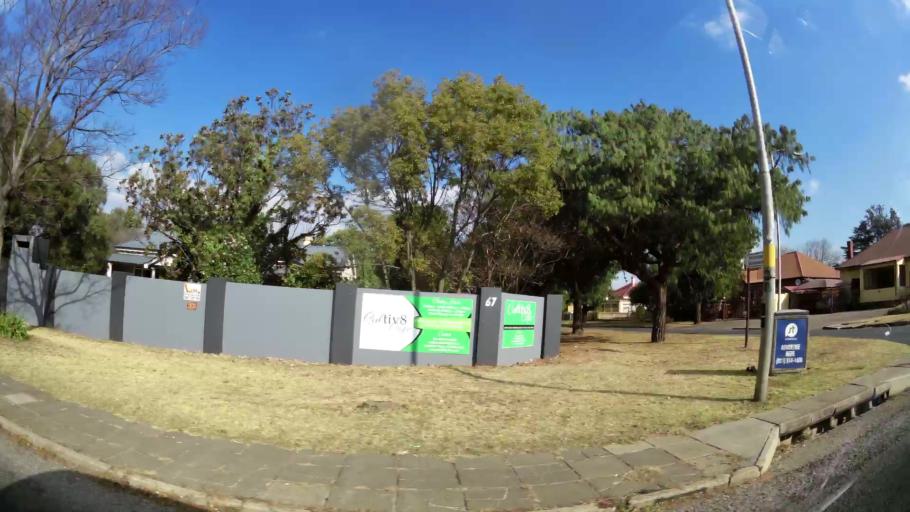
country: ZA
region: Gauteng
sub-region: West Rand District Municipality
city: Krugersdorp
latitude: -26.0874
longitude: 27.7731
